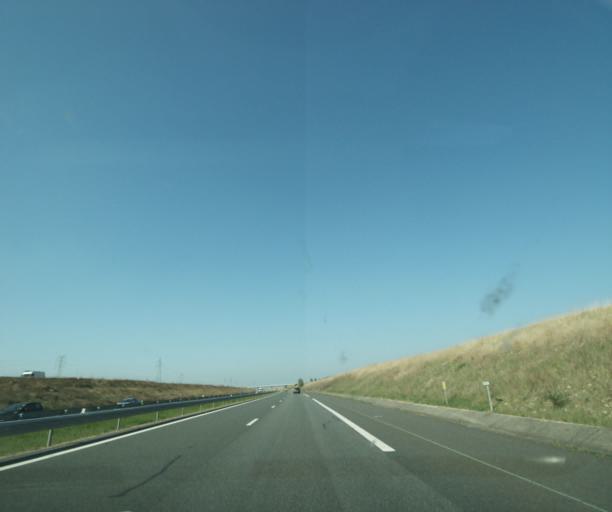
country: FR
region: Centre
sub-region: Departement du Loiret
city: Pannes
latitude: 48.0107
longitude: 2.6804
